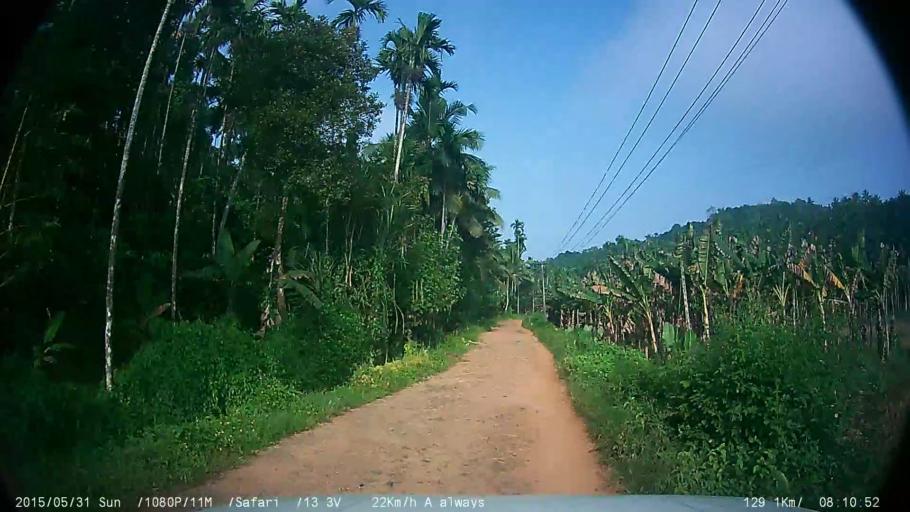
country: IN
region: Kerala
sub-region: Wayanad
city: Kalpetta
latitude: 11.6389
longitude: 76.0194
